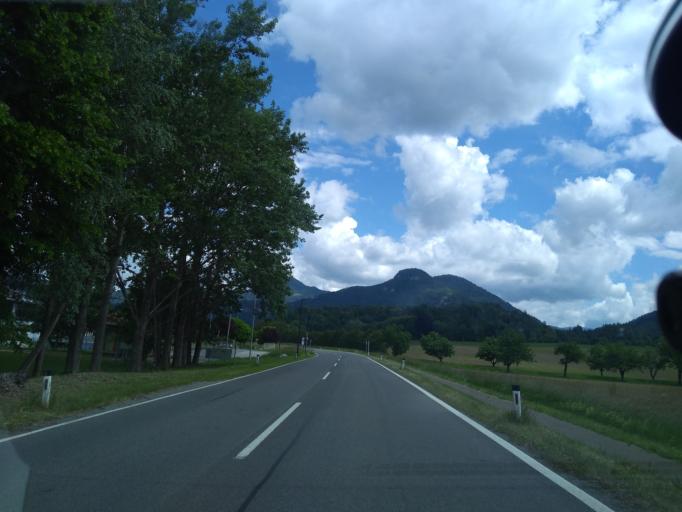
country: AT
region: Styria
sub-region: Politischer Bezirk Graz-Umgebung
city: Frohnleiten
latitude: 47.2546
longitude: 15.3202
